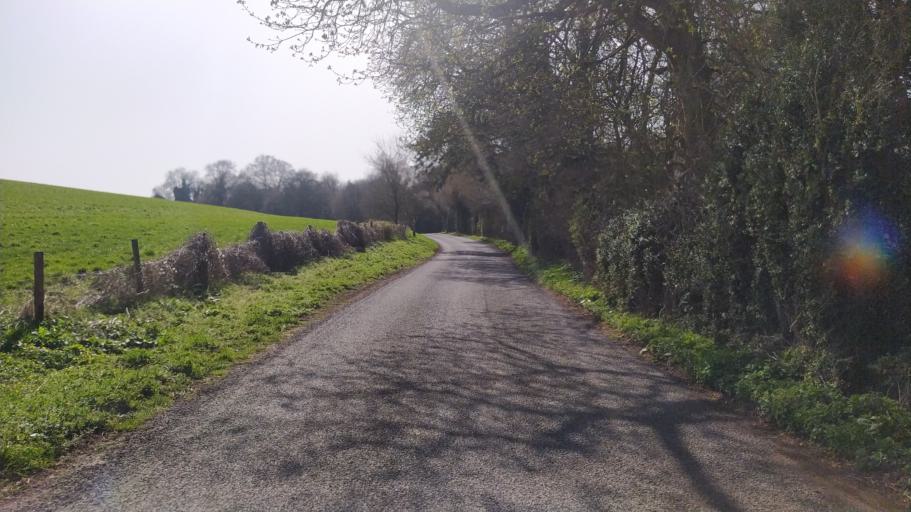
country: GB
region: England
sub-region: Hampshire
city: Kings Worthy
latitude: 51.0828
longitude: -1.2447
